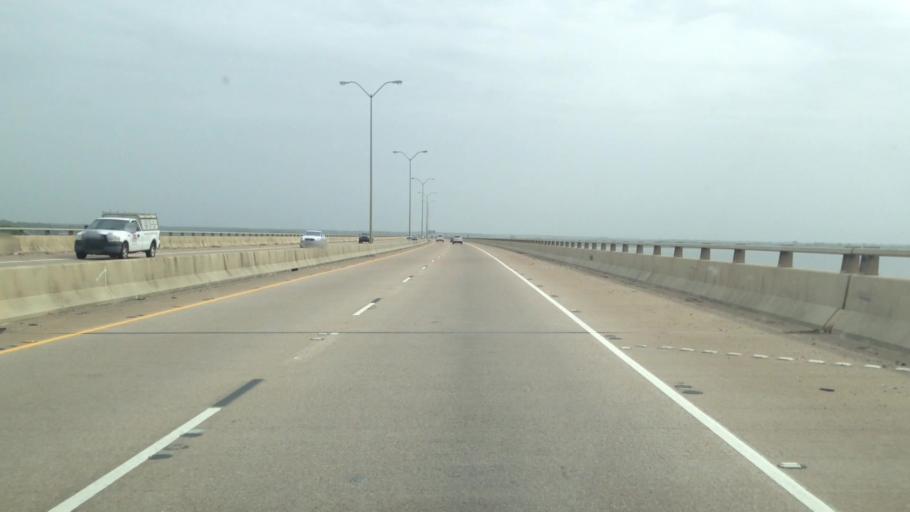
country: US
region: Louisiana
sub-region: Caddo Parish
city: Shreveport
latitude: 32.4962
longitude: -93.8207
